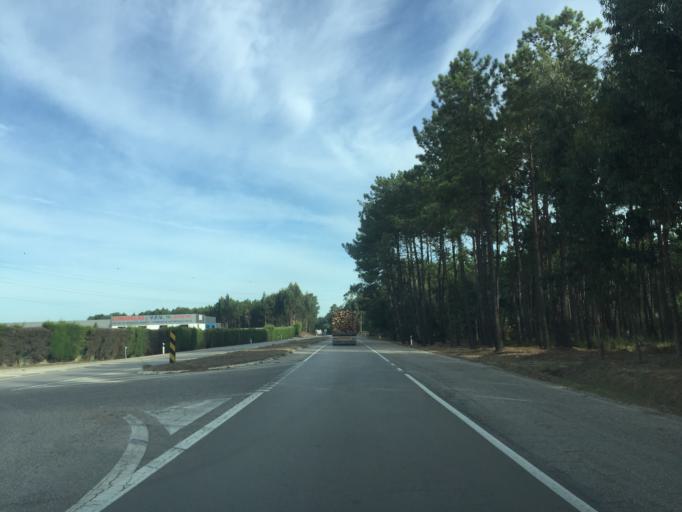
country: PT
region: Leiria
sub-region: Pombal
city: Lourical
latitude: 40.0089
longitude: -8.8065
